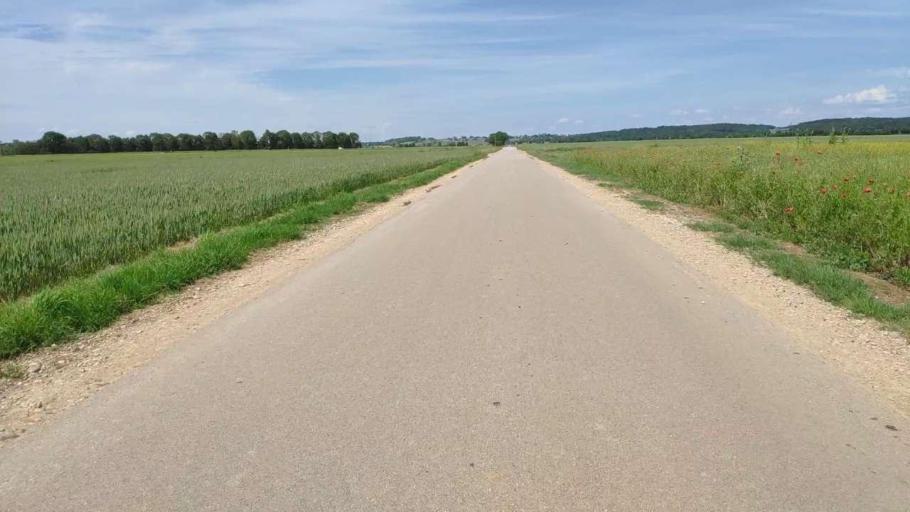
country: FR
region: Franche-Comte
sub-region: Departement du Jura
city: Bletterans
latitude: 46.7501
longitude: 5.4943
